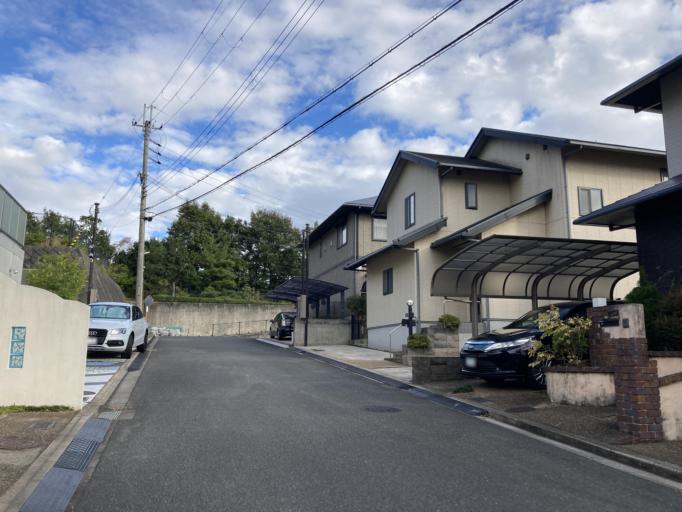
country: JP
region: Nara
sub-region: Ikoma-shi
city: Ikoma
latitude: 34.6785
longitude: 135.7141
